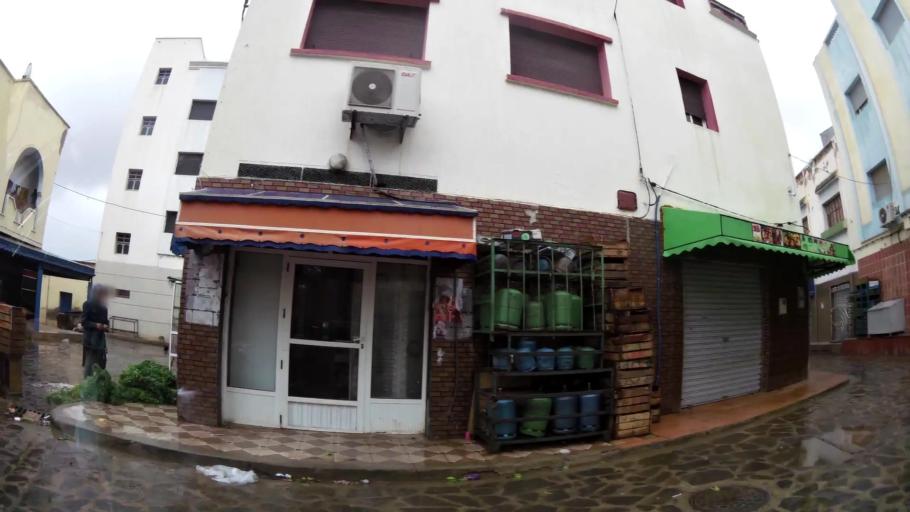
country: MA
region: Oriental
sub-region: Nador
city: Nador
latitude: 35.1726
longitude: -2.9380
